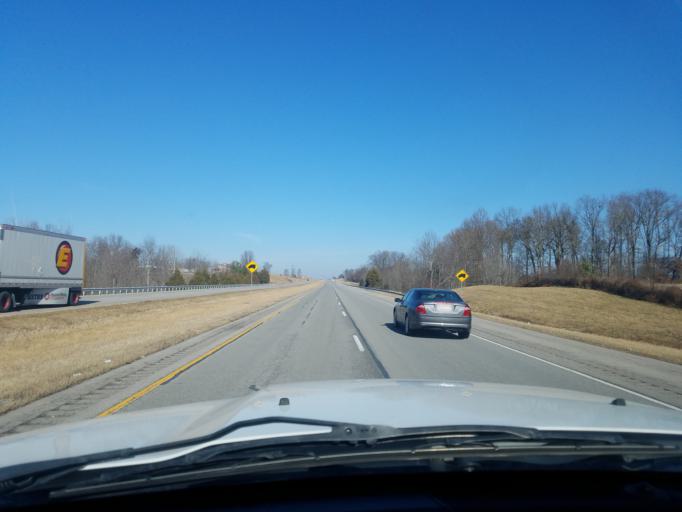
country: US
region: Kentucky
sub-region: Hardin County
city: Elizabethtown
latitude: 37.6458
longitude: -85.8379
